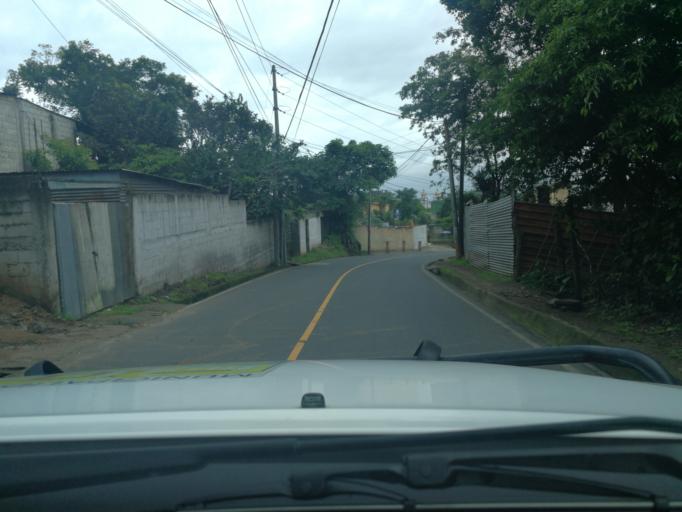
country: GT
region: Guatemala
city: Santa Catarina Pinula
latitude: 14.5514
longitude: -90.5076
